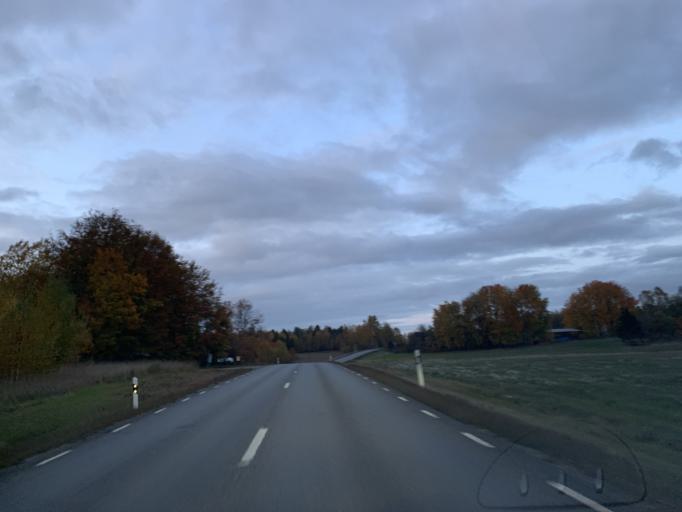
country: SE
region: Stockholm
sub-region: Nynashamns Kommun
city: Osmo
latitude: 59.0266
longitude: 17.7982
